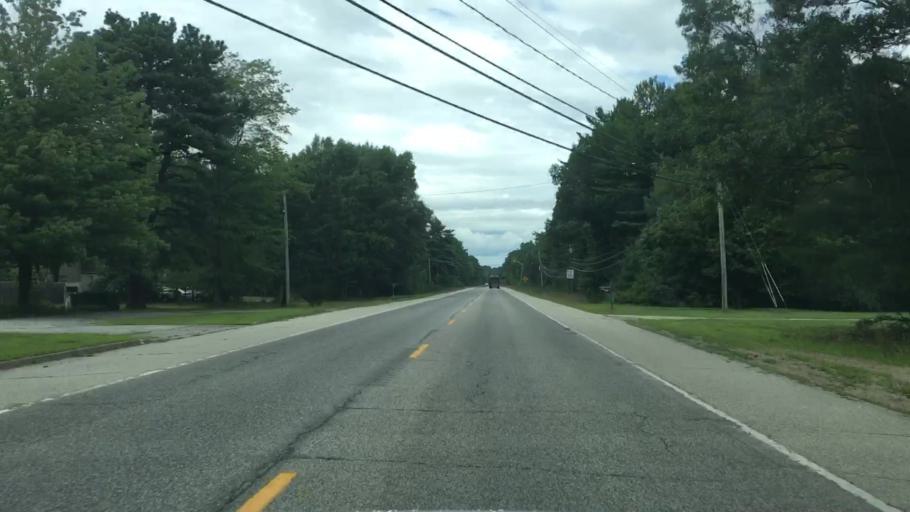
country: US
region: Maine
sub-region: York County
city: North Berwick
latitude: 43.3413
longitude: -70.7320
